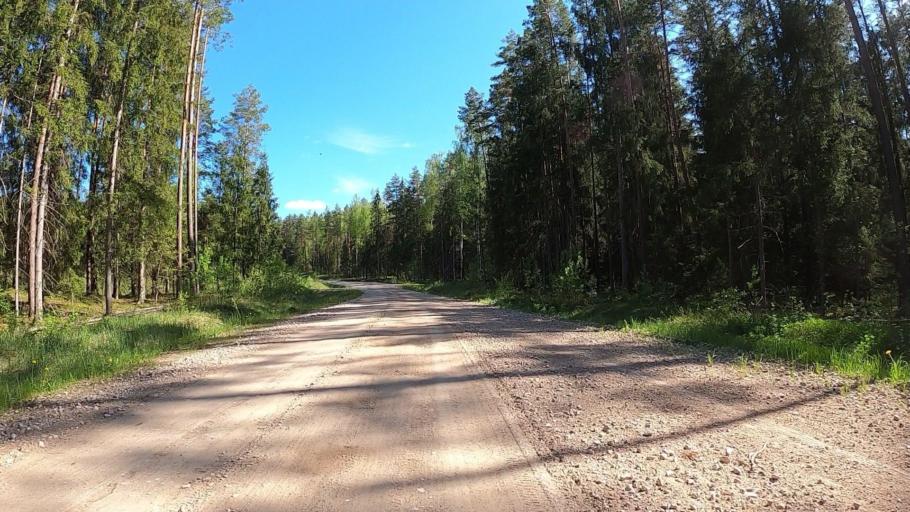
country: LV
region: Baldone
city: Baldone
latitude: 56.7706
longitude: 24.3743
